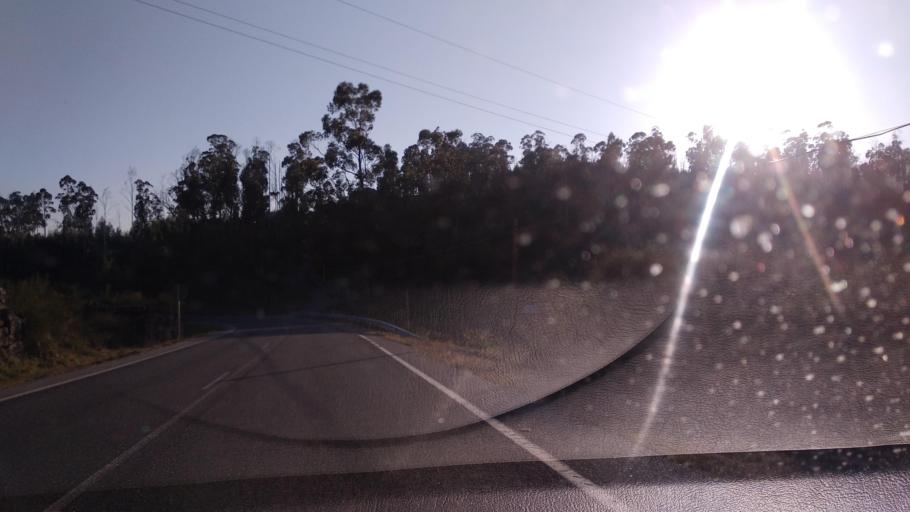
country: ES
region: Galicia
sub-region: Provincia de Pontevedra
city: Ponte Caldelas
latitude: 42.3603
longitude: -8.5399
